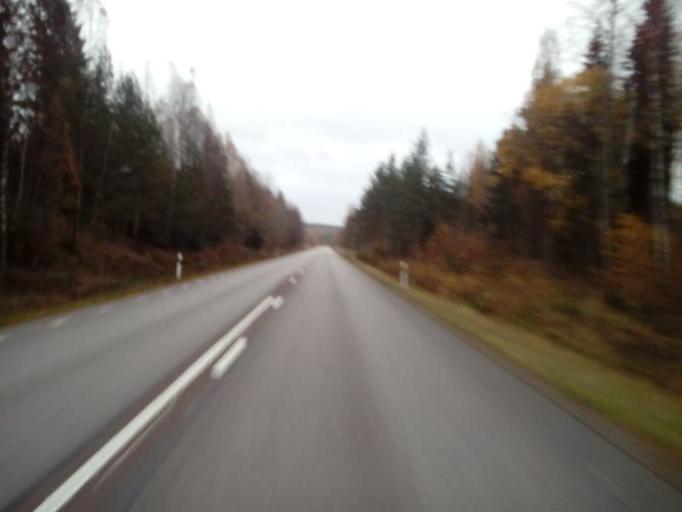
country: SE
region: OErebro
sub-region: Degerfors Kommun
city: Degerfors
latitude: 59.1872
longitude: 14.4697
